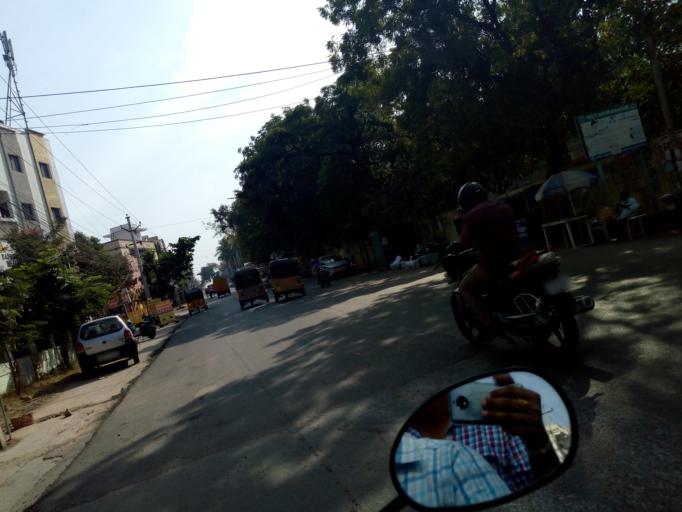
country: IN
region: Telangana
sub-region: Rangareddi
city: Gaddi Annaram
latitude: 17.3581
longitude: 78.5363
